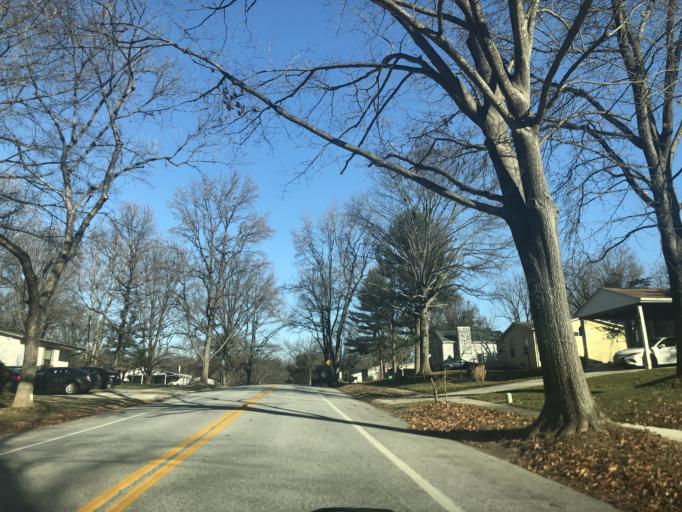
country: US
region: Maryland
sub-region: Howard County
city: Columbia
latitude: 39.2003
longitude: -76.8392
